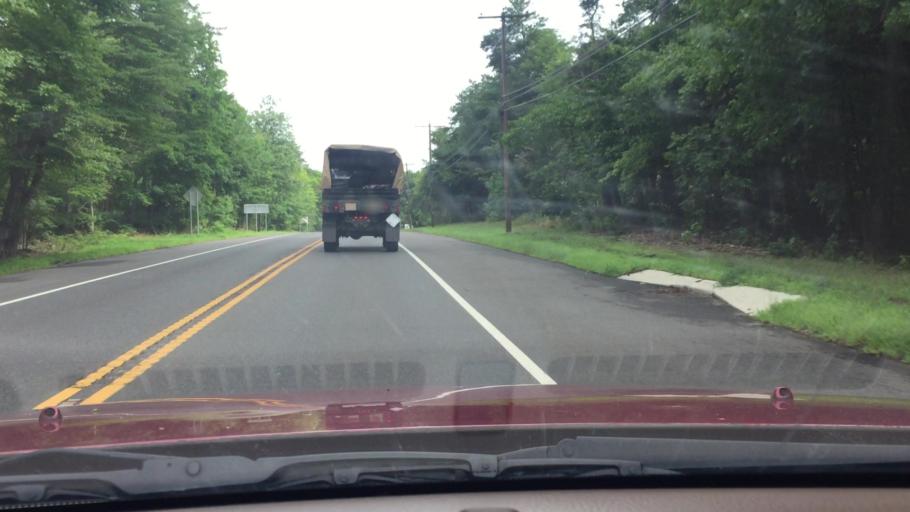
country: US
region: New Jersey
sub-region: Burlington County
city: Fort Dix
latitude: 40.0321
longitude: -74.6420
